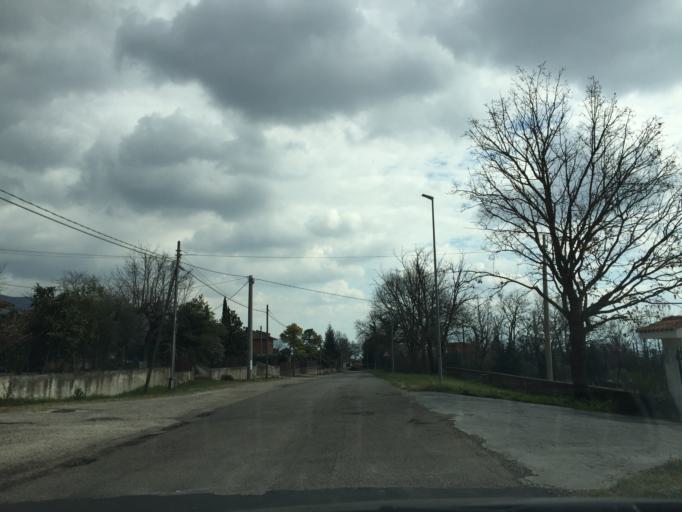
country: IT
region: Latium
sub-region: Provincia di Frosinone
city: Piedimonte San Germano Alta
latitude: 41.5012
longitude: 13.7384
